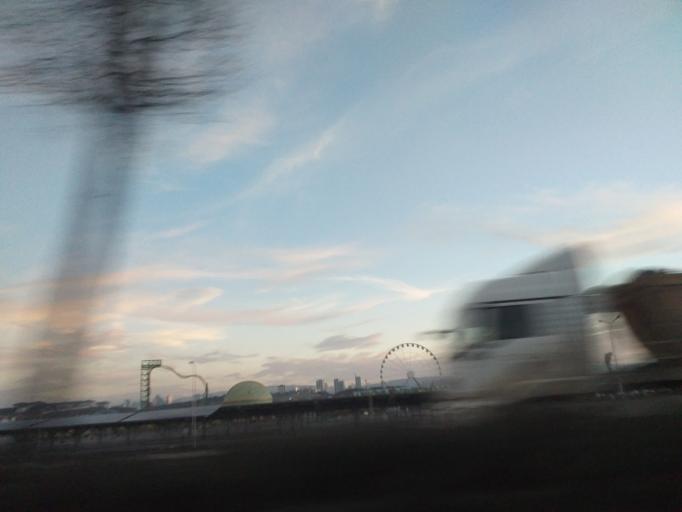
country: TR
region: Ankara
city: Batikent
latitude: 39.9465
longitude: 32.7794
